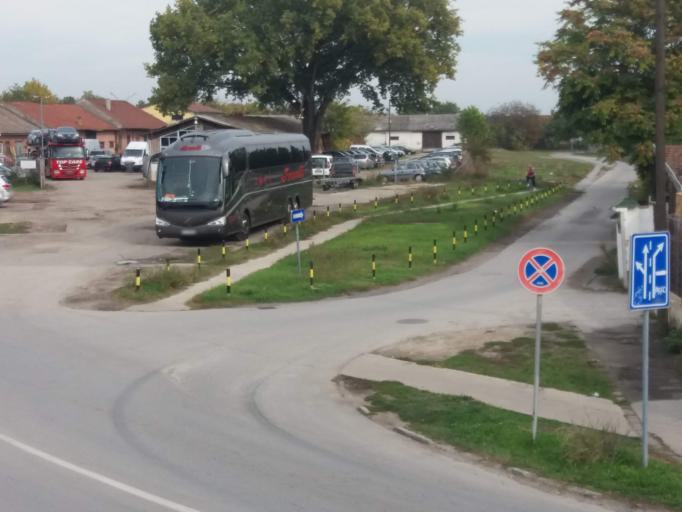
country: RS
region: Autonomna Pokrajina Vojvodina
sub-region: Severnobacki Okrug
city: Subotica
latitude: 46.1096
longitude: 19.6690
